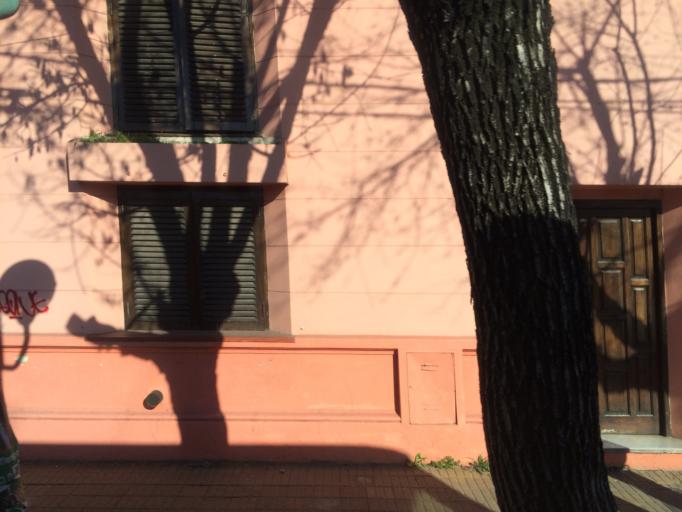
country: AR
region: Buenos Aires
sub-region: Partido de Lomas de Zamora
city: Lomas de Zamora
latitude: -34.7484
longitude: -58.3943
